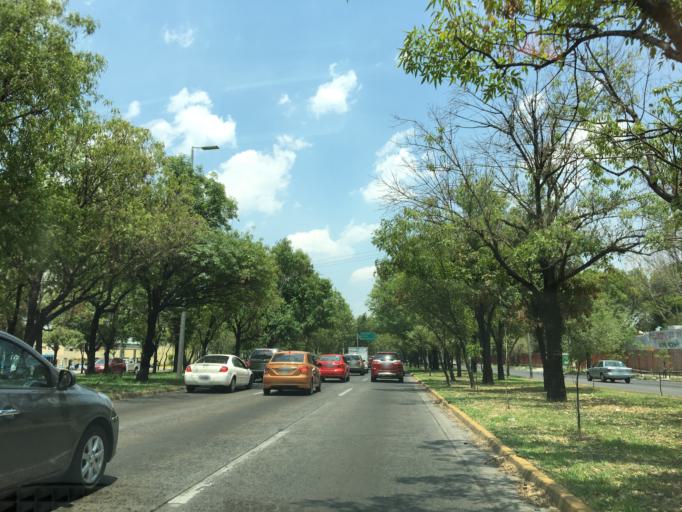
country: MX
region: Jalisco
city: Guadalajara
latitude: 20.6396
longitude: -103.3476
